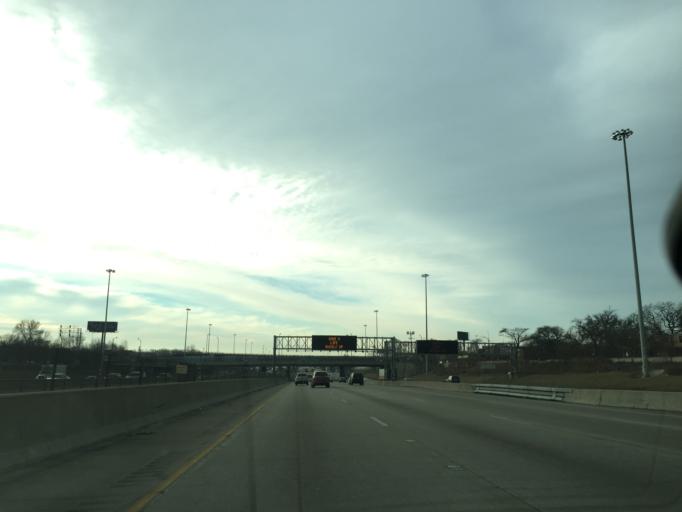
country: US
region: Illinois
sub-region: Cook County
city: Chicago
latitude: 41.8259
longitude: -87.6307
